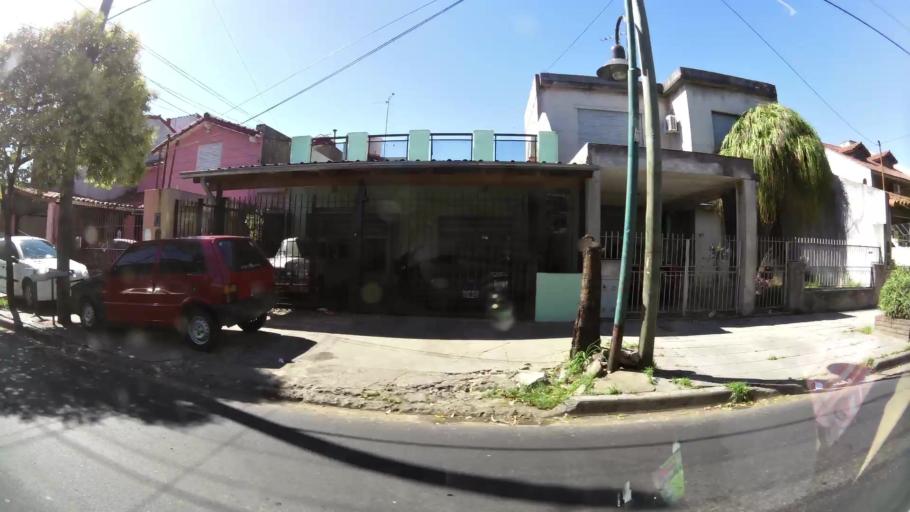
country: AR
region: Buenos Aires
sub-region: Partido de General San Martin
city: General San Martin
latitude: -34.5332
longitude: -58.5232
